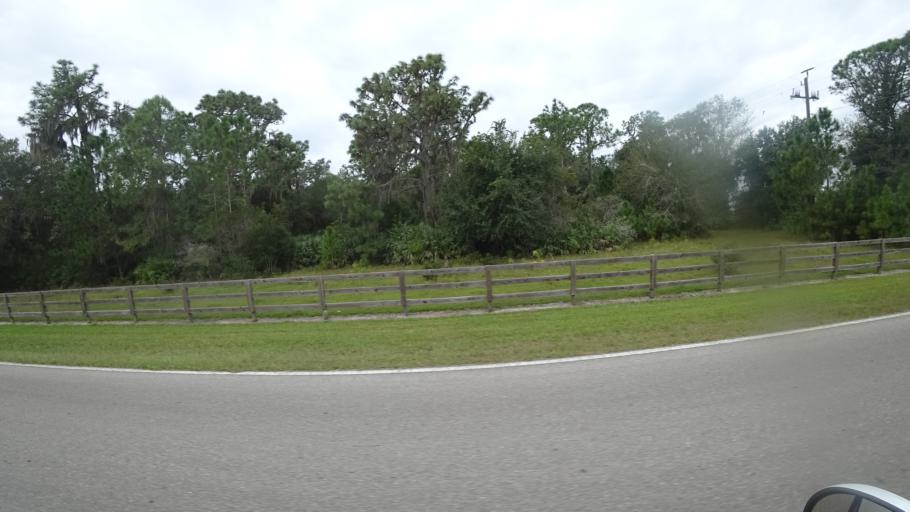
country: US
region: Florida
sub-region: Hillsborough County
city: Sun City Center
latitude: 27.6007
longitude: -82.3440
